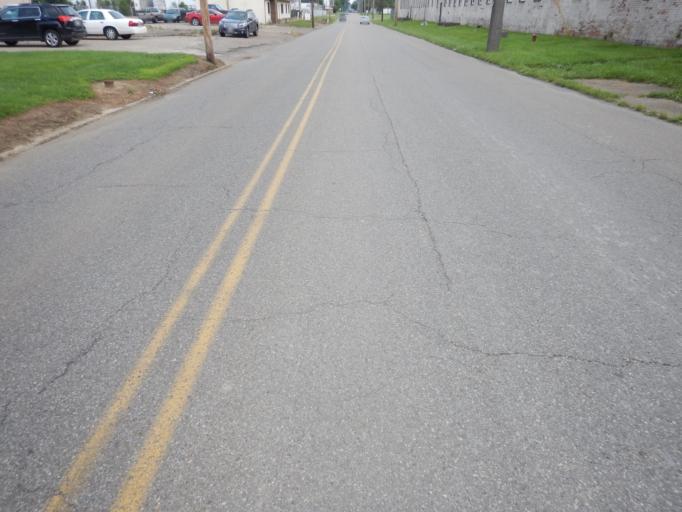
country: US
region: Ohio
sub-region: Muskingum County
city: South Zanesville
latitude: 39.9139
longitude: -82.0051
